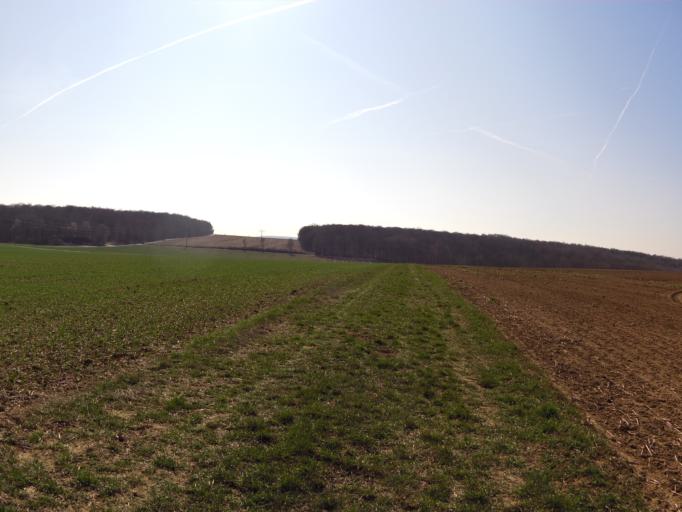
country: DE
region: Bavaria
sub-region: Regierungsbezirk Unterfranken
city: Rottendorf
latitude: 49.8162
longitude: 10.0265
